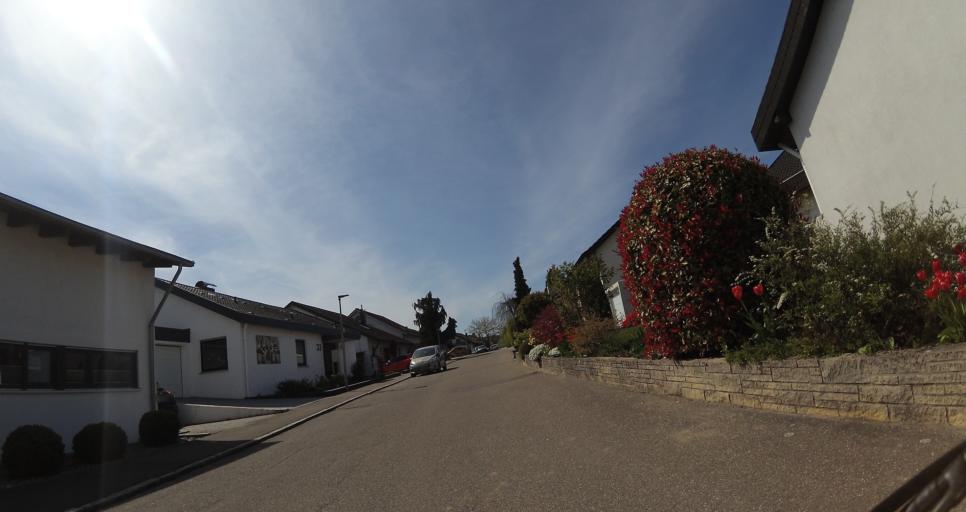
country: DE
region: Baden-Wuerttemberg
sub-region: Regierungsbezirk Stuttgart
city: Untereisesheim
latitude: 49.2106
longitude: 9.1956
